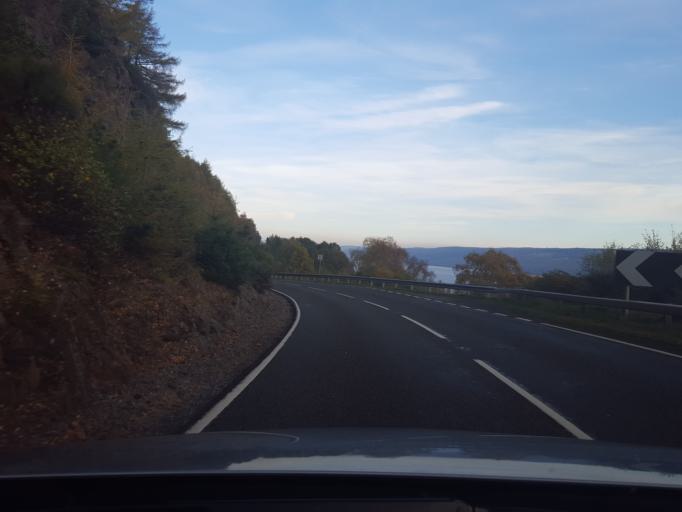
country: GB
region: Scotland
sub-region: Highland
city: Beauly
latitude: 57.3475
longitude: -4.4157
